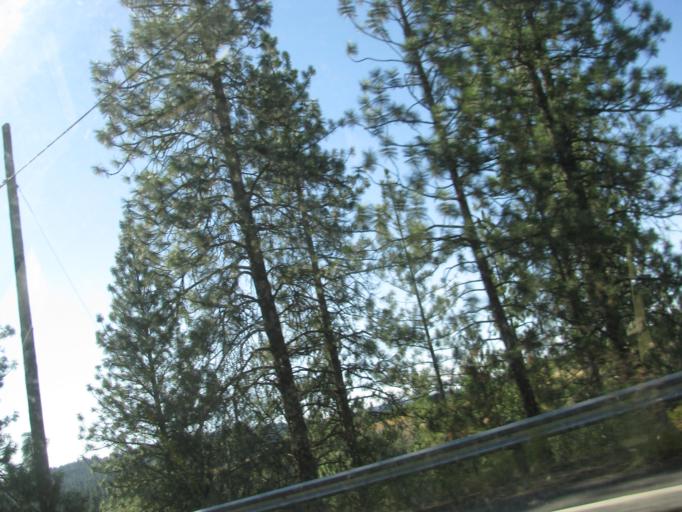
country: US
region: Washington
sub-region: Spokane County
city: Spokane
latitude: 47.6576
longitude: -117.4465
